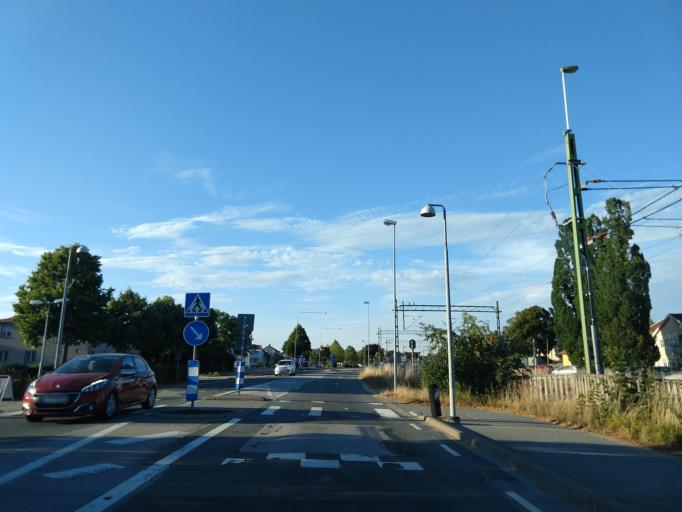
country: SE
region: Blekinge
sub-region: Ronneby Kommun
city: Brakne-Hoby
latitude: 56.2299
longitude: 15.1152
